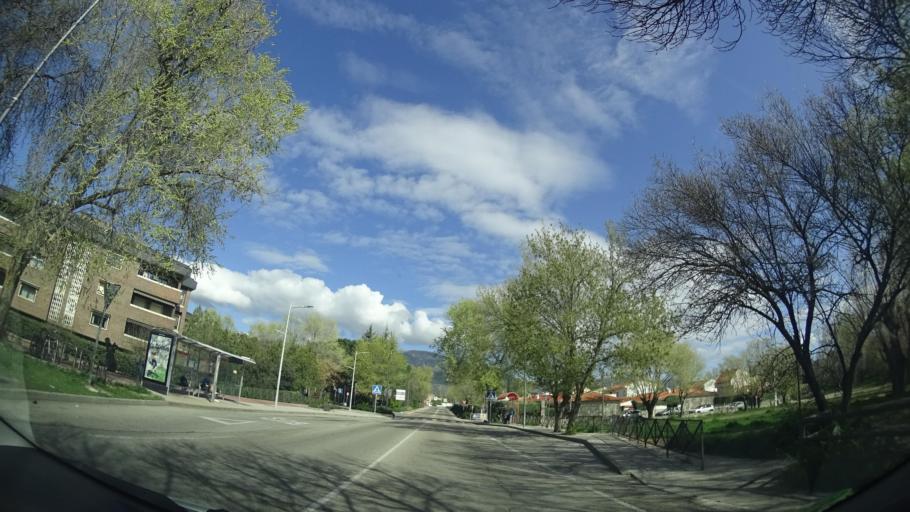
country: ES
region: Madrid
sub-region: Provincia de Madrid
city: Miraflores de la Sierra
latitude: 40.7525
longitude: -3.7822
